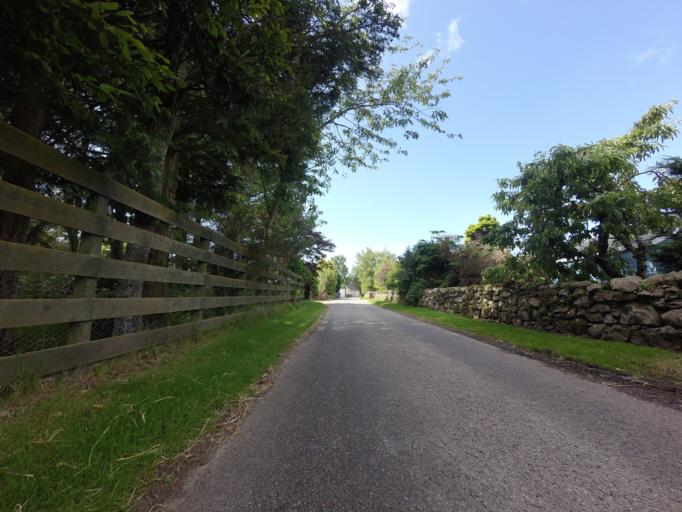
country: GB
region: Scotland
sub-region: Highland
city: Nairn
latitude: 57.5391
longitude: -3.8663
